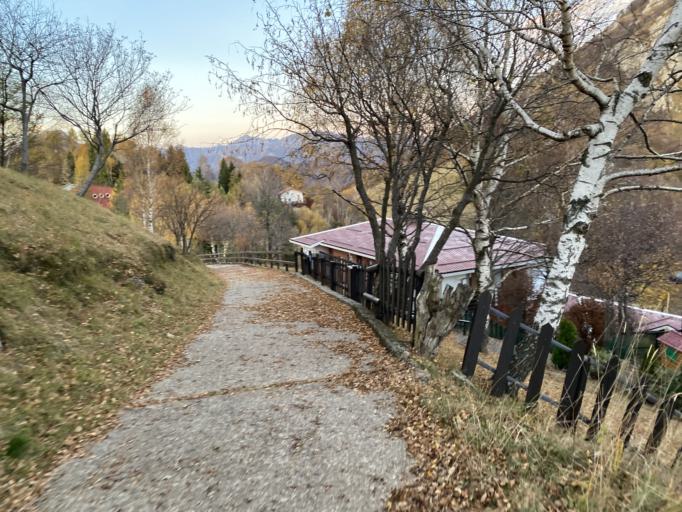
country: IT
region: Lombardy
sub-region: Provincia di Lecco
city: Morterone
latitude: 45.8634
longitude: 9.4475
